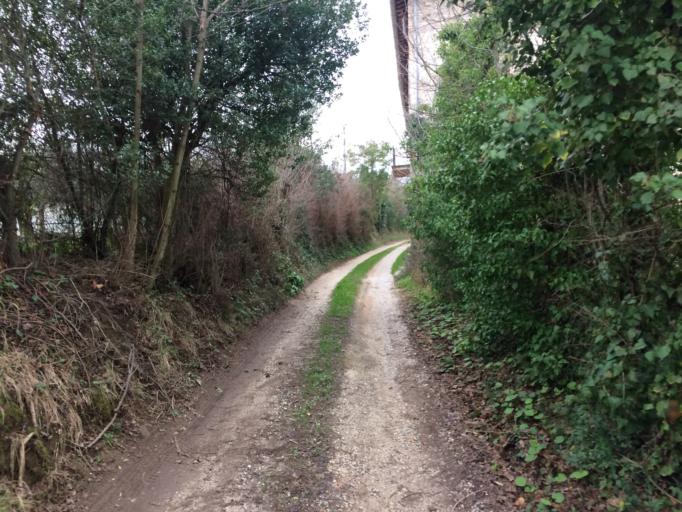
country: IT
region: Umbria
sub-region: Provincia di Perugia
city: Perugia
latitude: 43.1007
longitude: 12.4101
